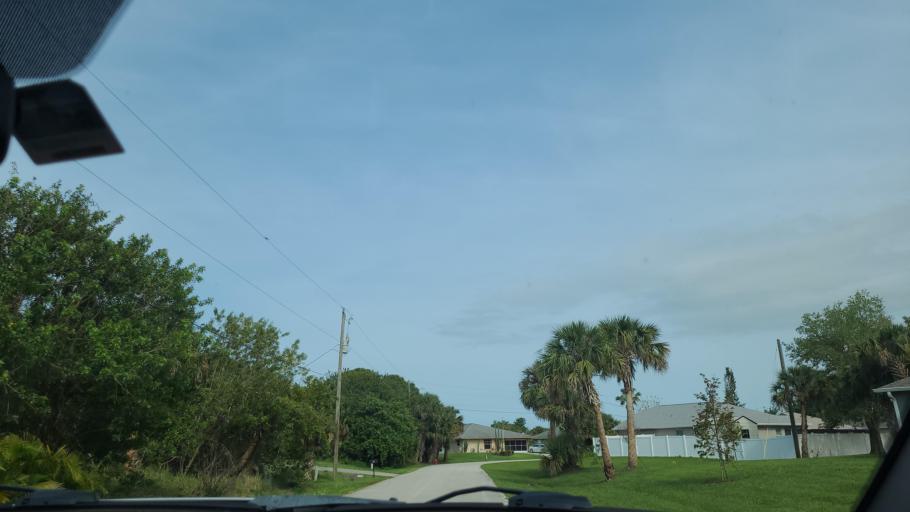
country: US
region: Florida
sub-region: Indian River County
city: Sebastian
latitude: 27.7700
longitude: -80.4756
